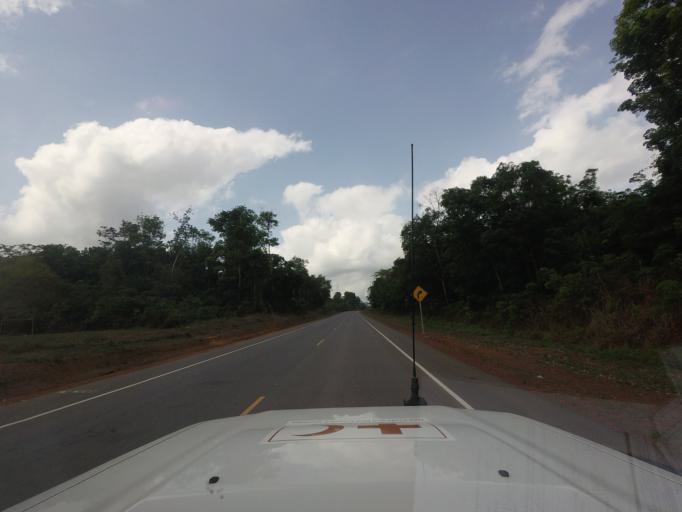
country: LR
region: Nimba
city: Sanniquellie
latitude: 7.1589
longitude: -9.0457
